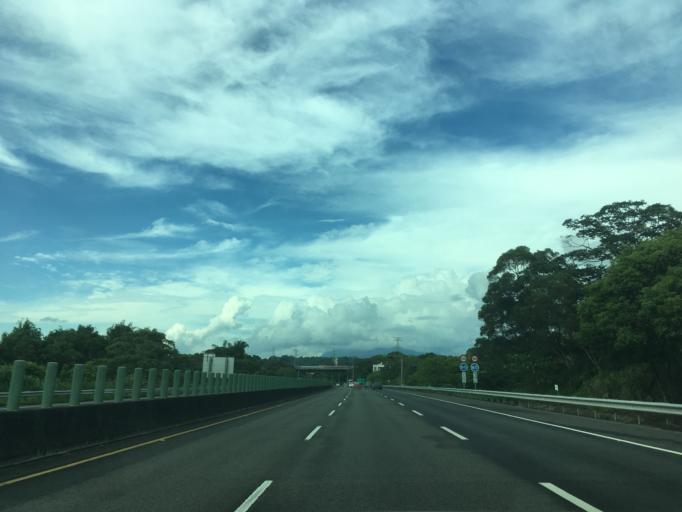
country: TW
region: Taiwan
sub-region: Chiayi
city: Jiayi Shi
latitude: 23.4598
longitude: 120.4930
